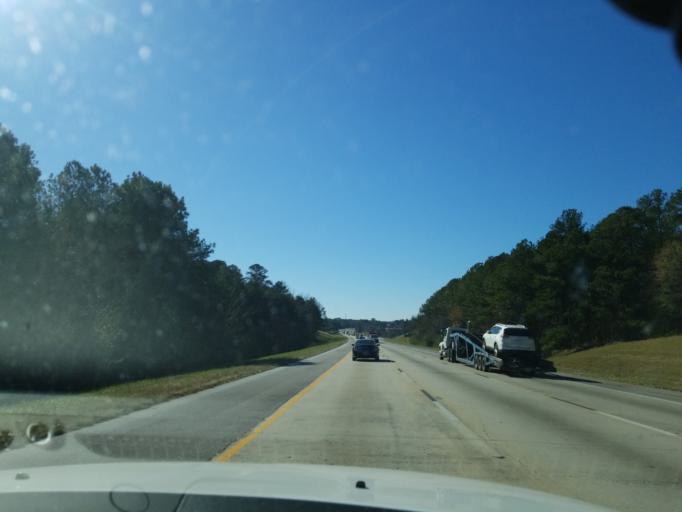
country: US
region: Alabama
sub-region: Jefferson County
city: Vestavia Hills
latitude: 33.4176
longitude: -86.7546
